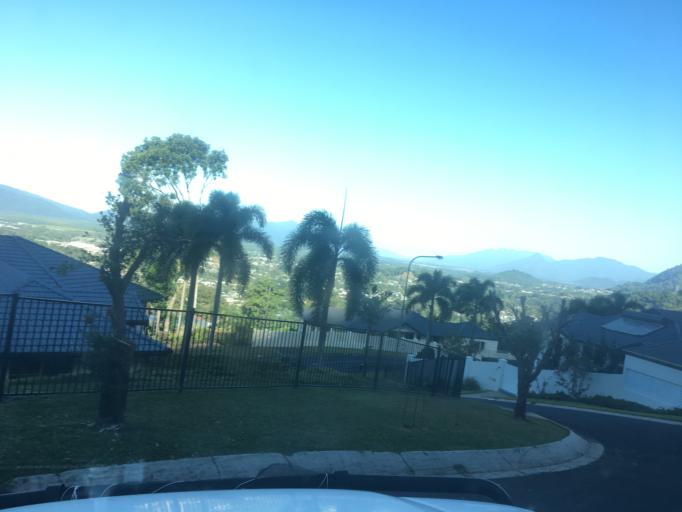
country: AU
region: Queensland
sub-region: Cairns
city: Woree
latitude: -16.9343
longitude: 145.7223
